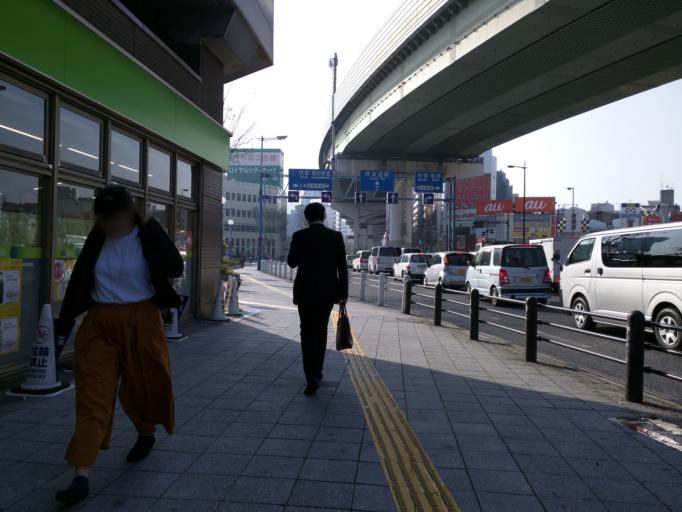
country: JP
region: Osaka
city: Osaka-shi
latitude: 34.6944
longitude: 135.4748
